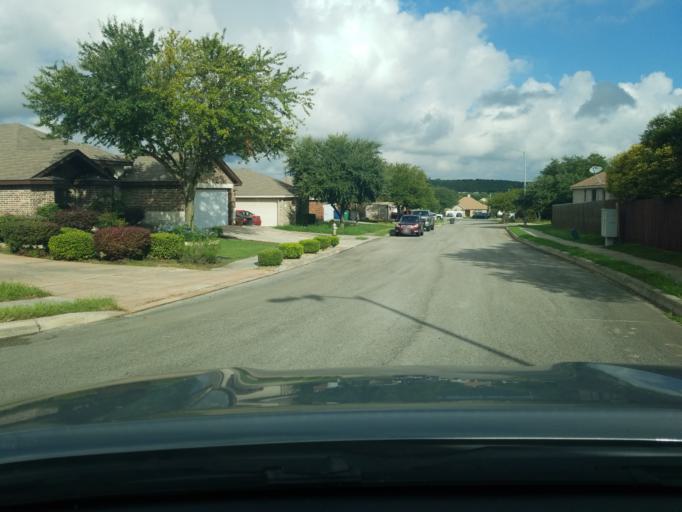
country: US
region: Texas
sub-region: Bexar County
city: Live Oak
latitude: 29.5757
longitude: -98.3597
